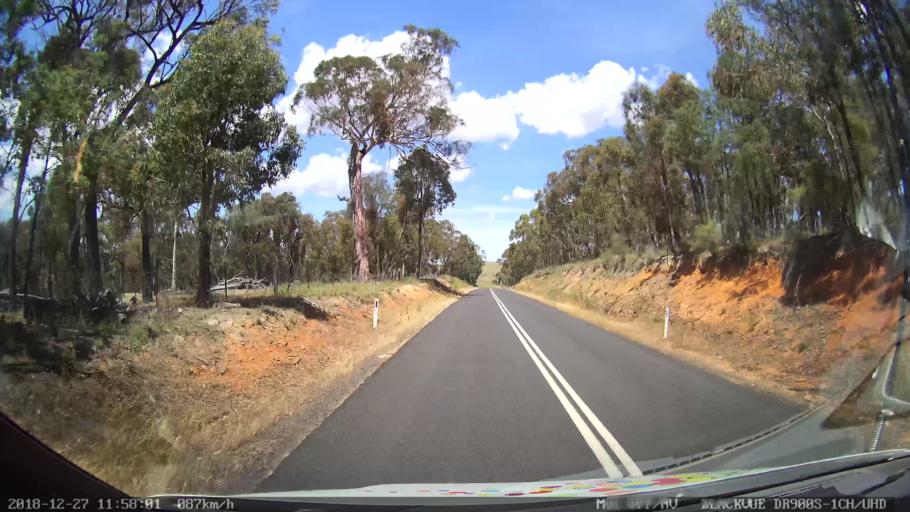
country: AU
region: New South Wales
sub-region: Blayney
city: Blayney
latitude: -33.7191
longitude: 149.3871
